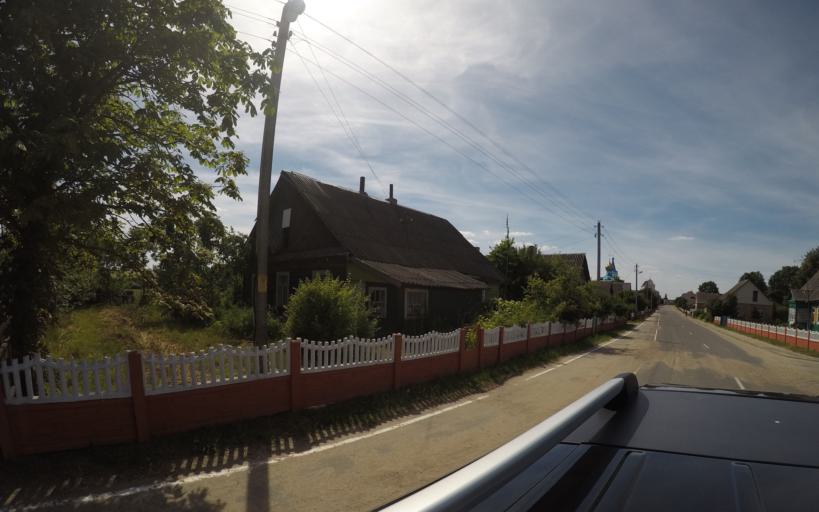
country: BY
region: Grodnenskaya
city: Hal'shany
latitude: 54.2551
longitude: 26.0161
